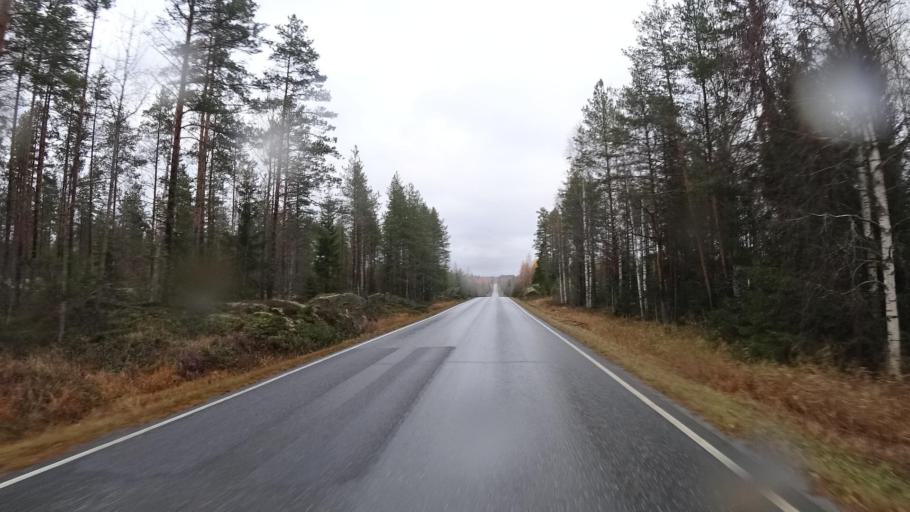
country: FI
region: North Karelia
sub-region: Joensuu
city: Polvijaervi
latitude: 63.0853
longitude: 29.5862
